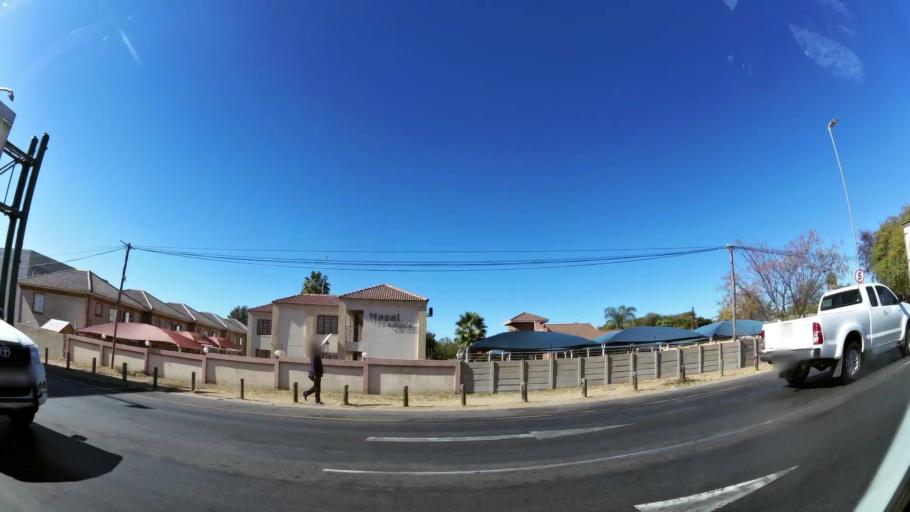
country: ZA
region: Limpopo
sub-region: Capricorn District Municipality
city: Polokwane
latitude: -23.9167
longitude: 29.4427
